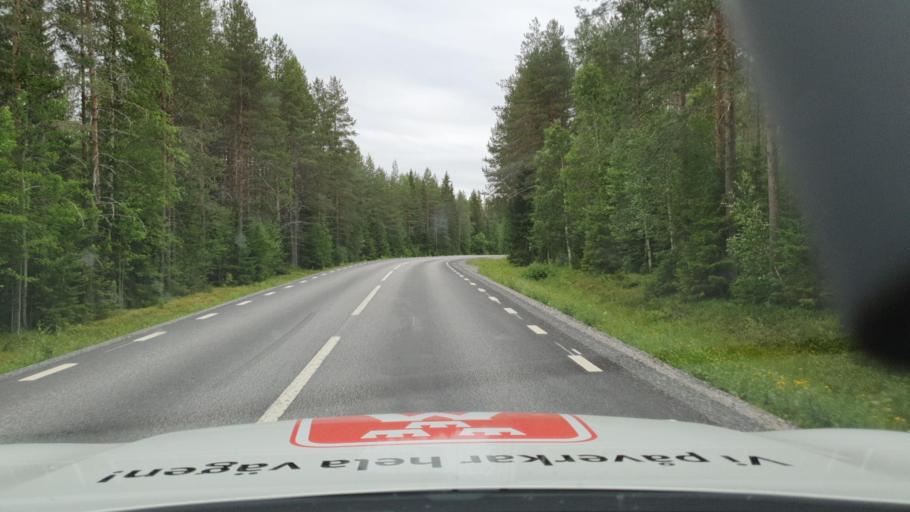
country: SE
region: Vaesterbotten
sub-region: Vannas Kommun
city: Vaennaes
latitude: 63.7281
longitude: 19.6513
